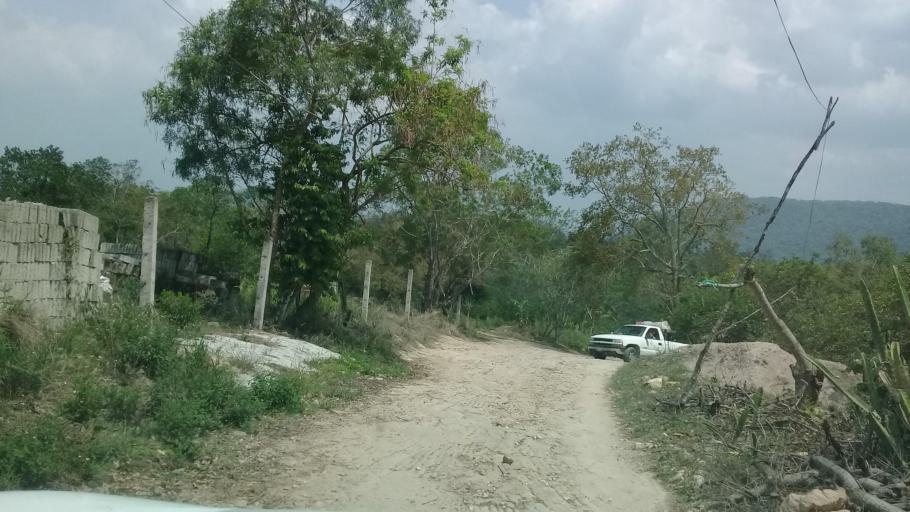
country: MX
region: Veracruz
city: Jalcomulco
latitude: 19.3880
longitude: -96.7915
